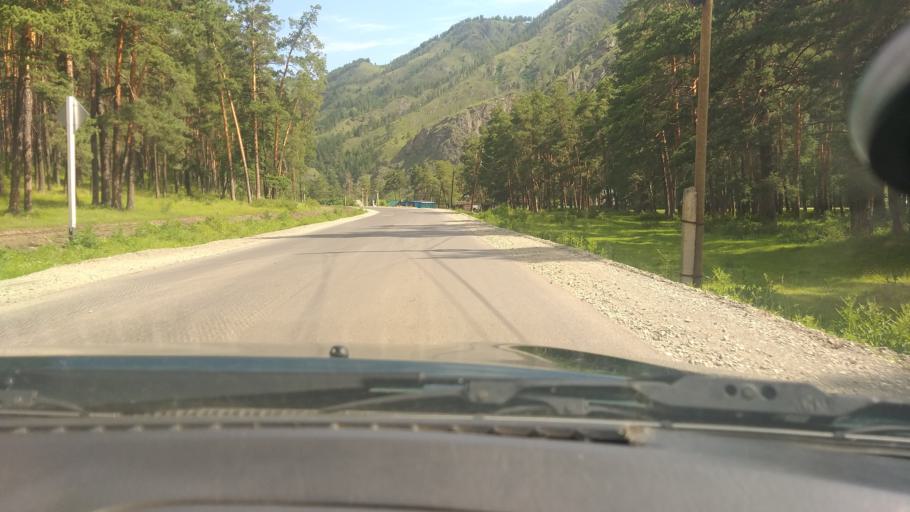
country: RU
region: Altay
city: Chemal
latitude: 51.3957
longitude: 86.0229
